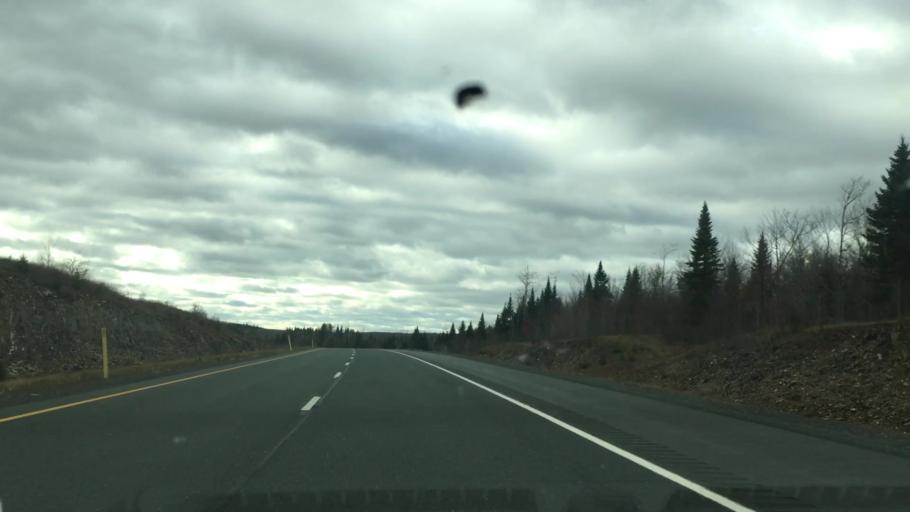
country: US
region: Maine
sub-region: Aroostook County
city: Easton
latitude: 46.6093
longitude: -67.7428
